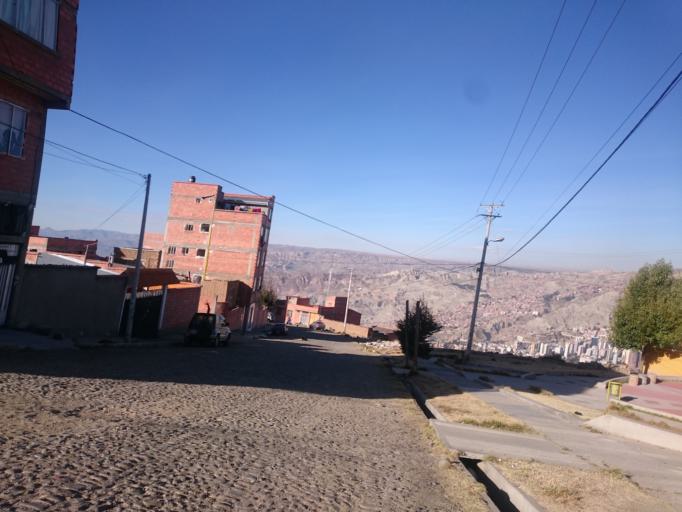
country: BO
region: La Paz
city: La Paz
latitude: -16.4905
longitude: -68.1070
